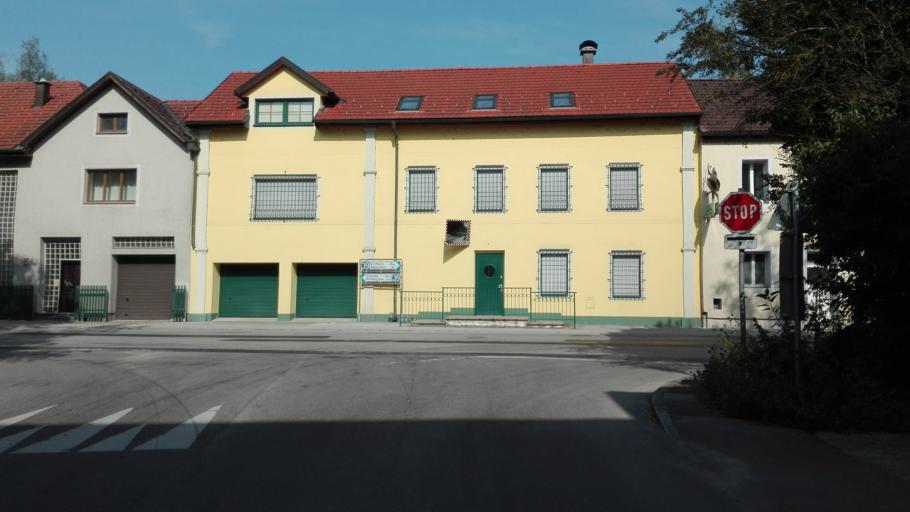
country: AT
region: Lower Austria
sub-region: Politischer Bezirk Sankt Polten
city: Kirchberg an der Pielach
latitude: 48.0401
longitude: 15.4504
